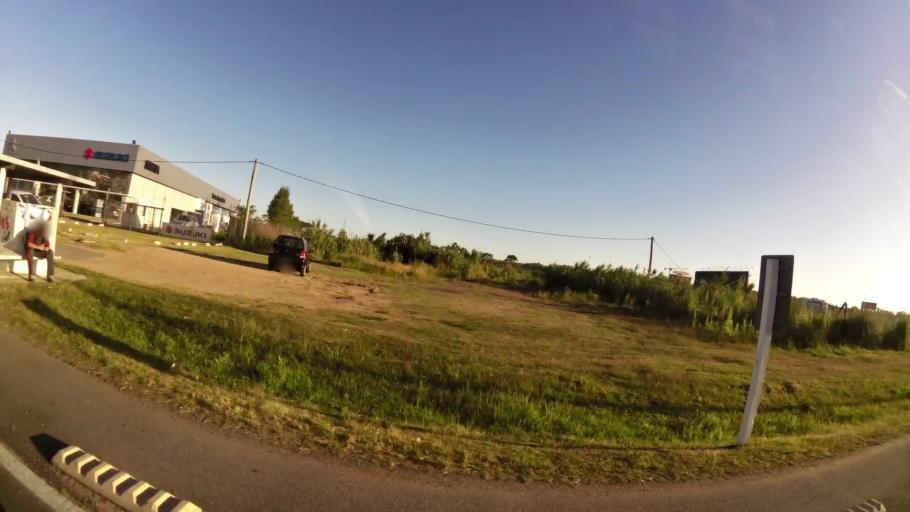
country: UY
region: Canelones
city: Barra de Carrasco
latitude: -34.8453
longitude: -56.0221
